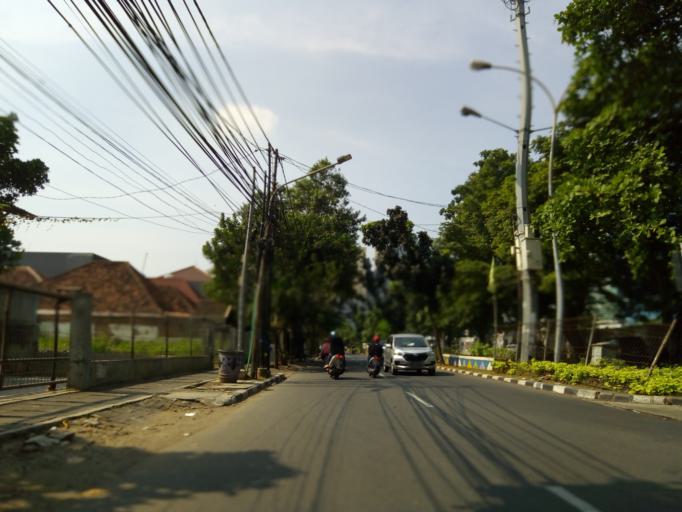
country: ID
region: Jakarta Raya
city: Jakarta
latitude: -6.2095
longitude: 106.8333
